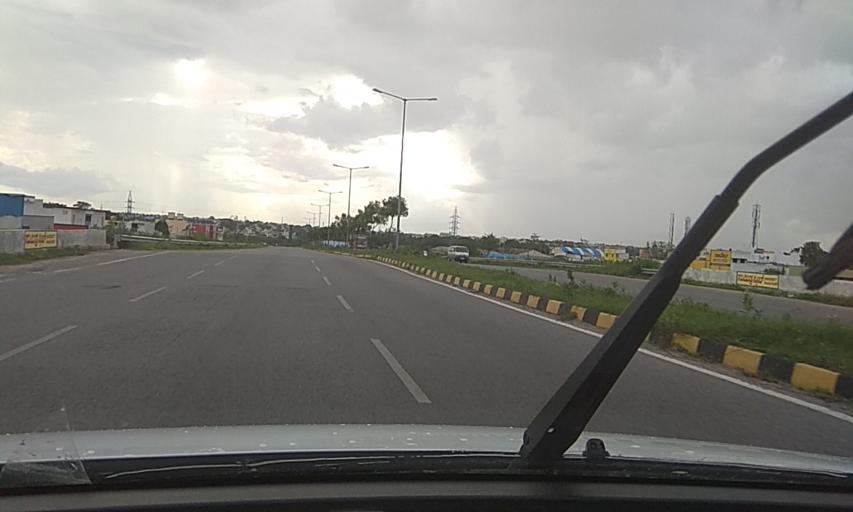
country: IN
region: Karnataka
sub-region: Mysore
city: Mysore
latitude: 12.2615
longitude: 76.6623
